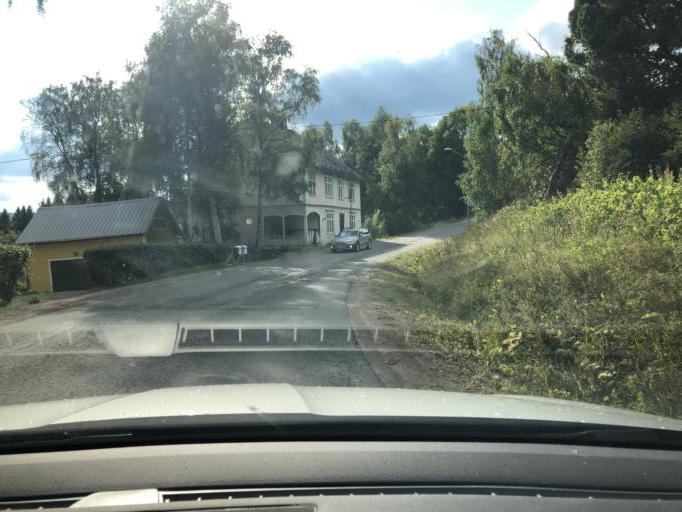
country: SE
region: Vaesternorrland
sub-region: Solleftea Kommun
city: Solleftea
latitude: 63.2115
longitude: 17.1885
